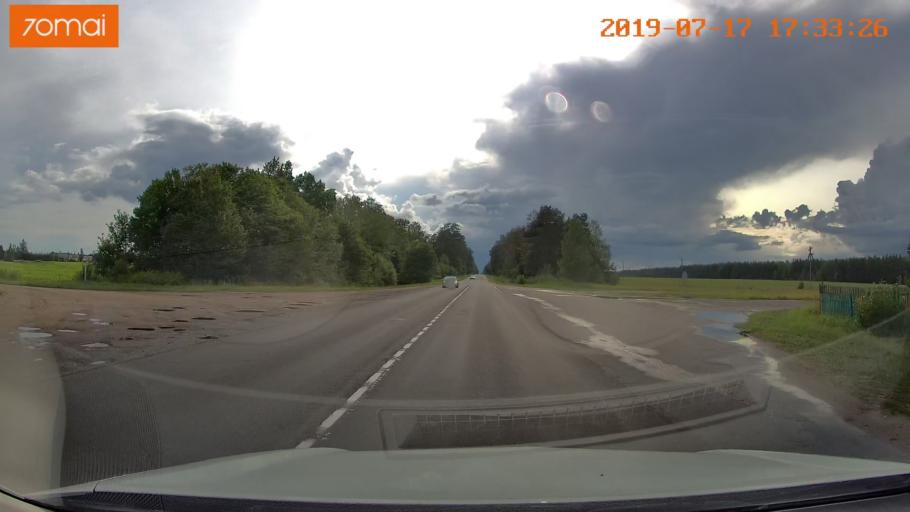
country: BY
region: Mogilev
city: Babruysk
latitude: 53.1114
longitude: 29.0922
